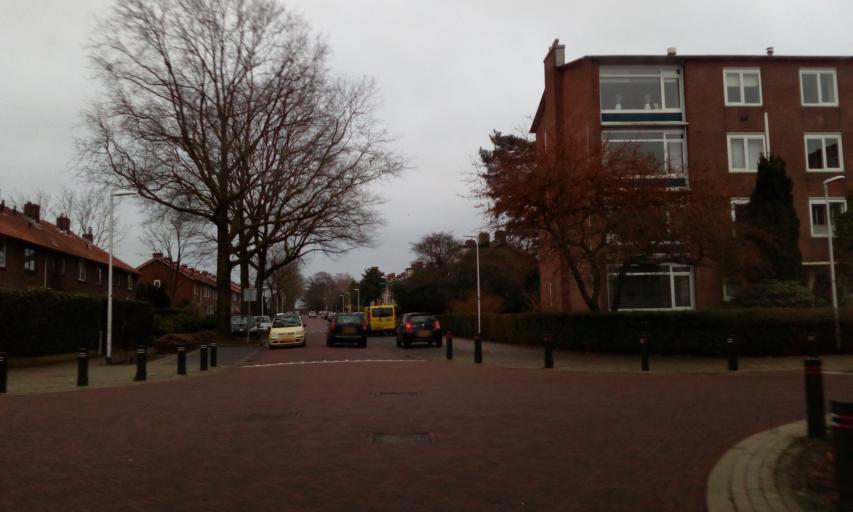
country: NL
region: North Holland
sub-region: Gemeente Bussum
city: Bussum
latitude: 52.2640
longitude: 5.1711
